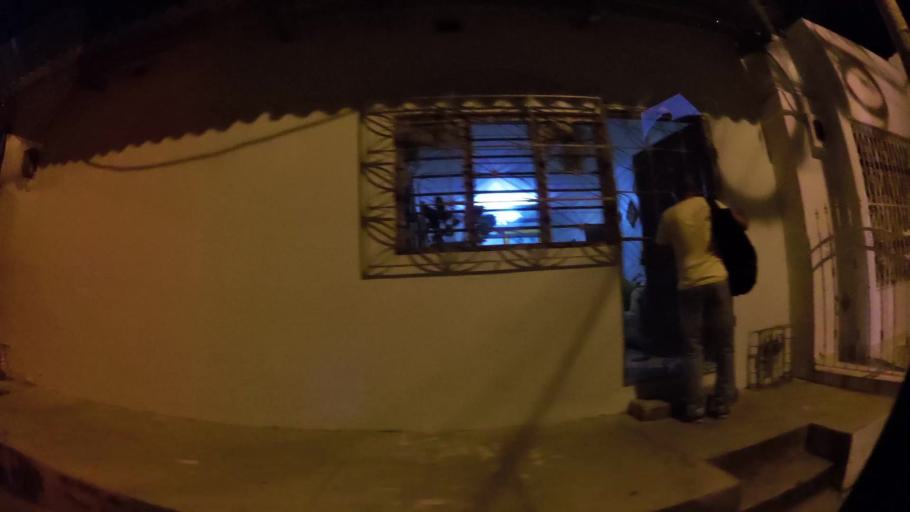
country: CO
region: Bolivar
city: Cartagena
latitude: 10.4108
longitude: -75.5200
